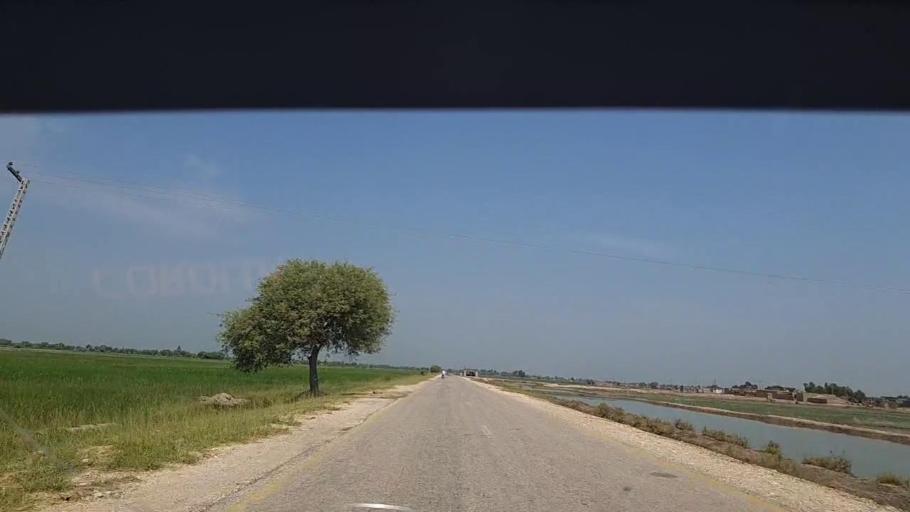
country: PK
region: Sindh
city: Rustam jo Goth
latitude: 28.0947
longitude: 68.8007
